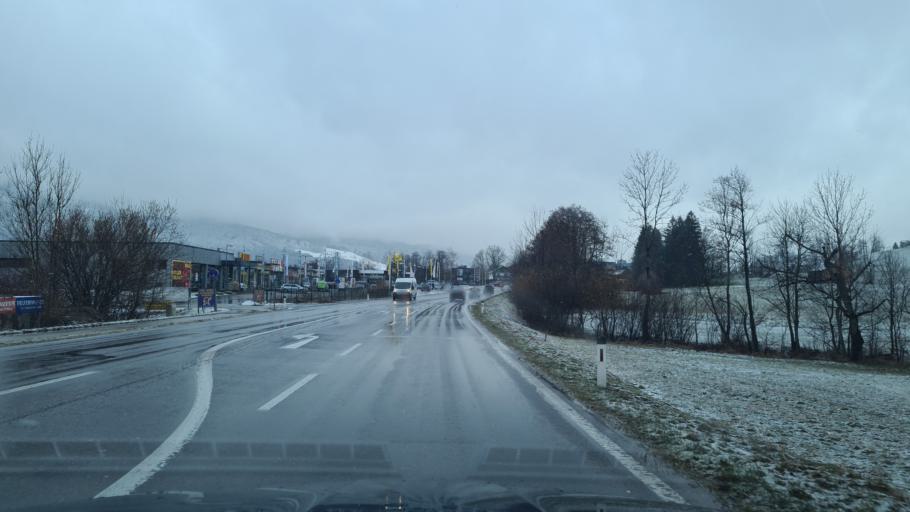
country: AT
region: Upper Austria
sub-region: Politischer Bezirk Vocklabruck
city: Mondsee
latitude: 47.8671
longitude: 13.3276
